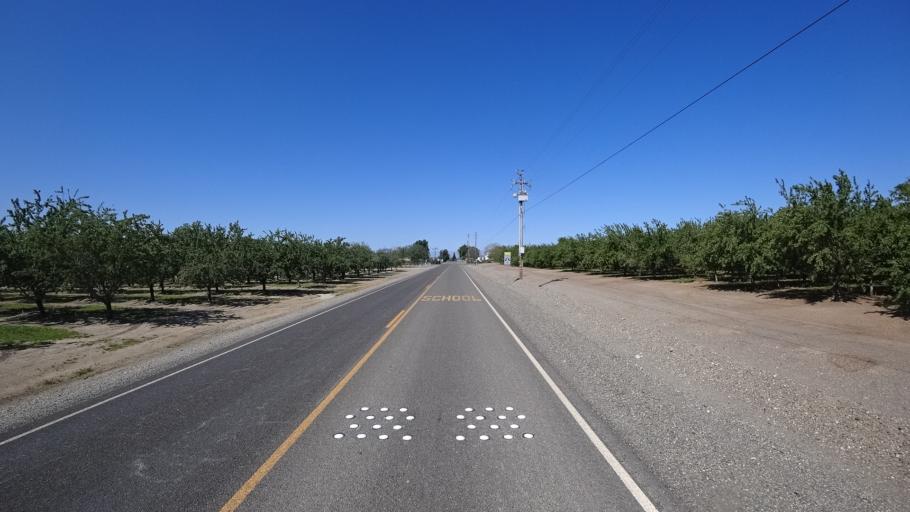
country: US
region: California
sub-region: Glenn County
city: Hamilton City
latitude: 39.7104
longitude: -122.1022
